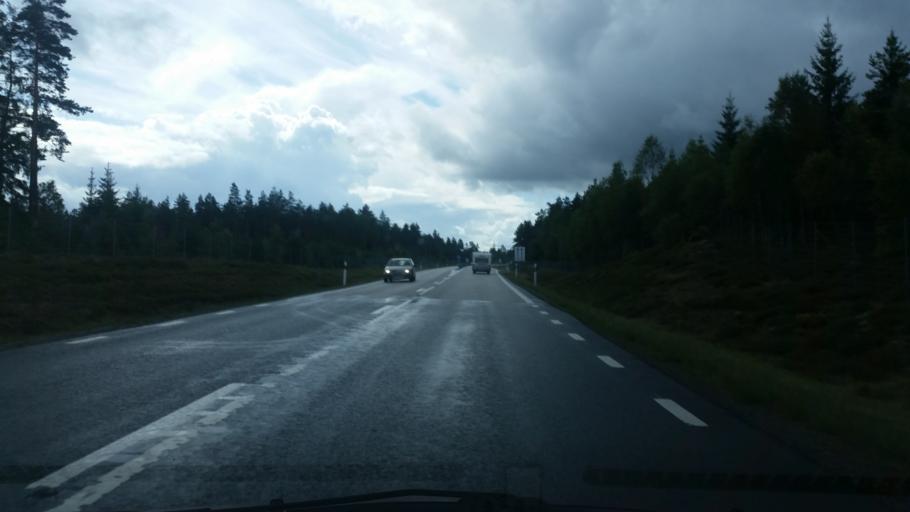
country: SE
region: Joenkoeping
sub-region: Gislaveds Kommun
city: Gislaved
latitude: 57.3524
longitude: 13.5574
